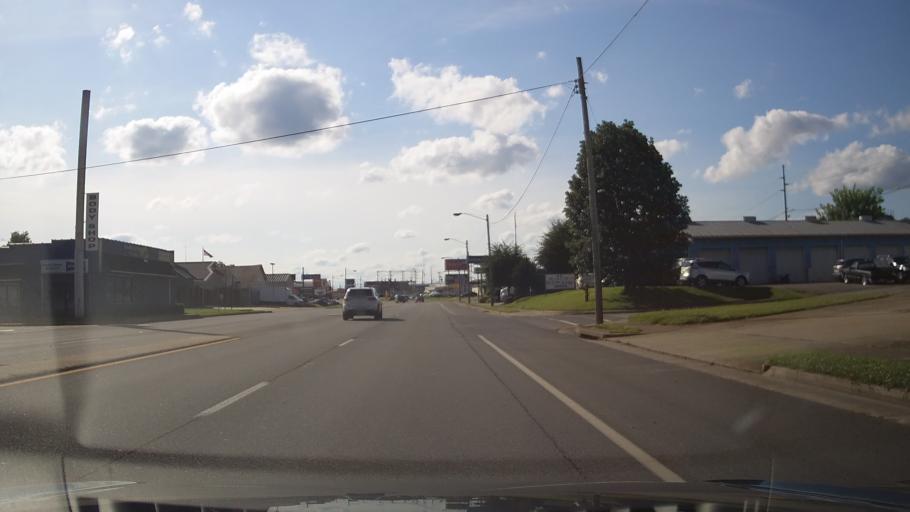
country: US
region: Kentucky
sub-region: Boyd County
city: Ashland
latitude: 38.4715
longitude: -82.6233
